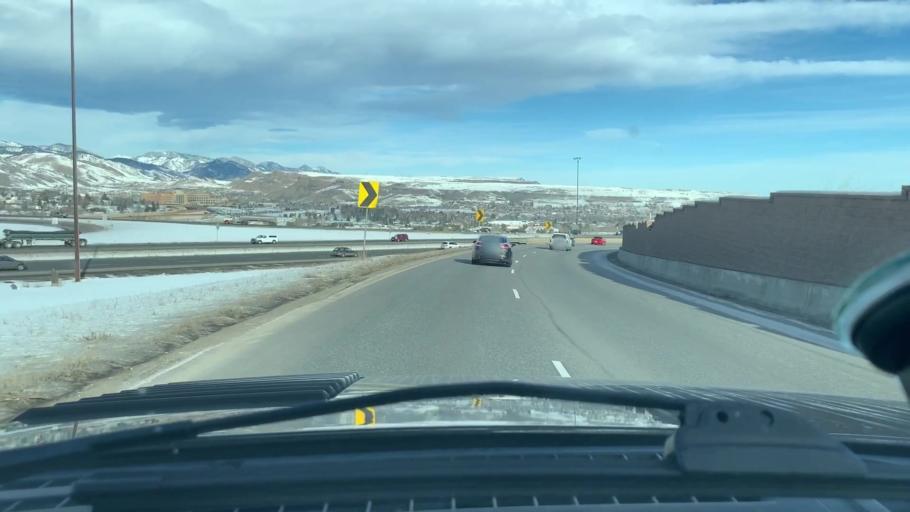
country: US
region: Colorado
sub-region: Jefferson County
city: West Pleasant View
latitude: 39.7136
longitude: -105.1918
